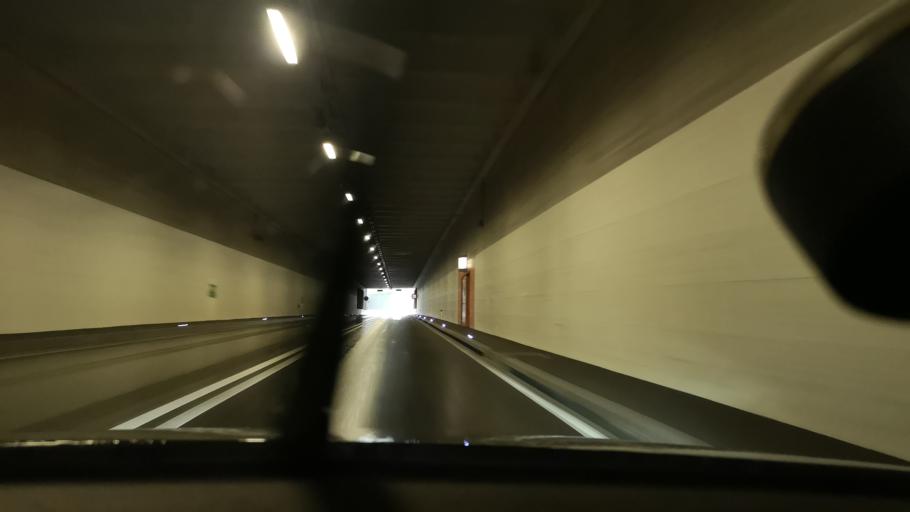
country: CH
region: Neuchatel
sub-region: Boudry District
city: Auvernier
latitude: 46.9859
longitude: 6.8729
